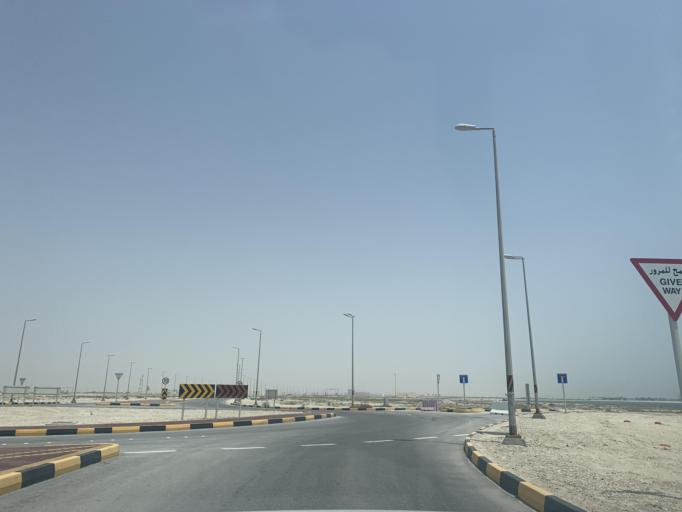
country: BH
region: Central Governorate
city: Dar Kulayb
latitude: 25.8326
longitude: 50.5936
